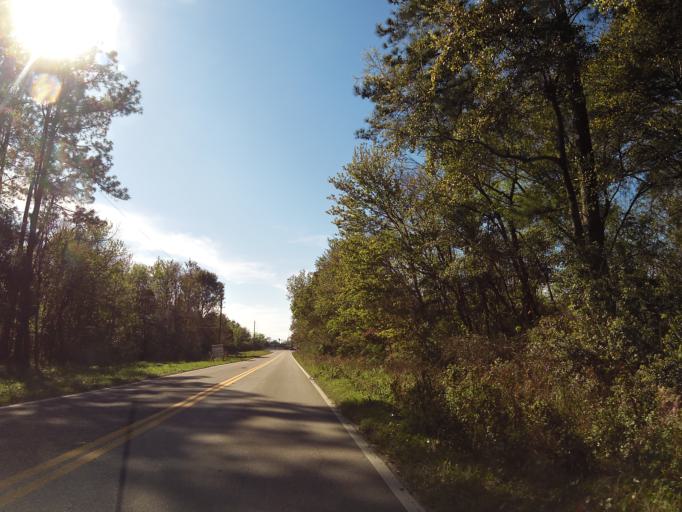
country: US
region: Florida
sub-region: Duval County
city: Jacksonville
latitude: 30.3765
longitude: -81.6480
